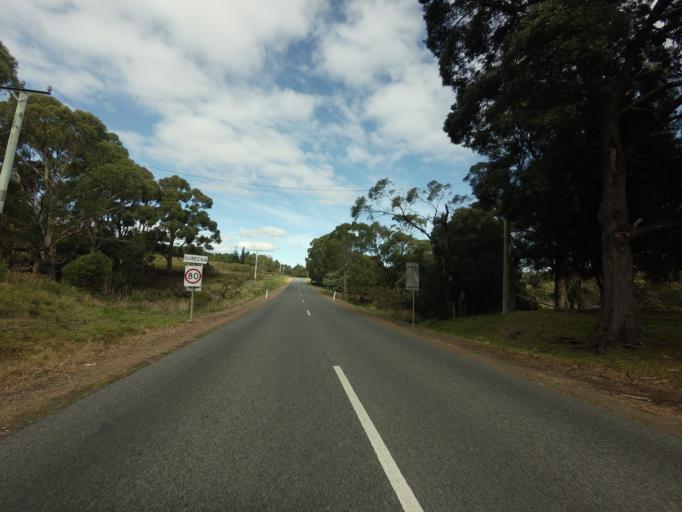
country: AU
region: Tasmania
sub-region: Clarence
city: Sandford
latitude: -43.0846
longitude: 147.7376
